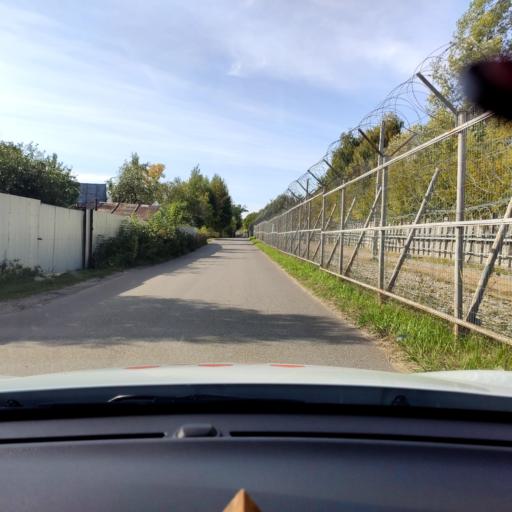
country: RU
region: Tatarstan
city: Staroye Arakchino
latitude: 55.8081
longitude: 49.0243
